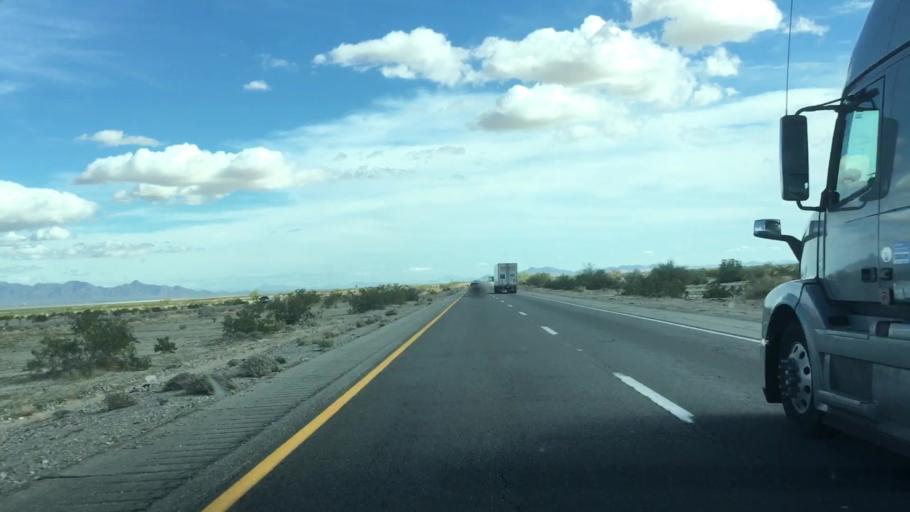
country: US
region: California
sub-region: Riverside County
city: Mesa Verde
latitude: 33.6467
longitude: -115.1230
